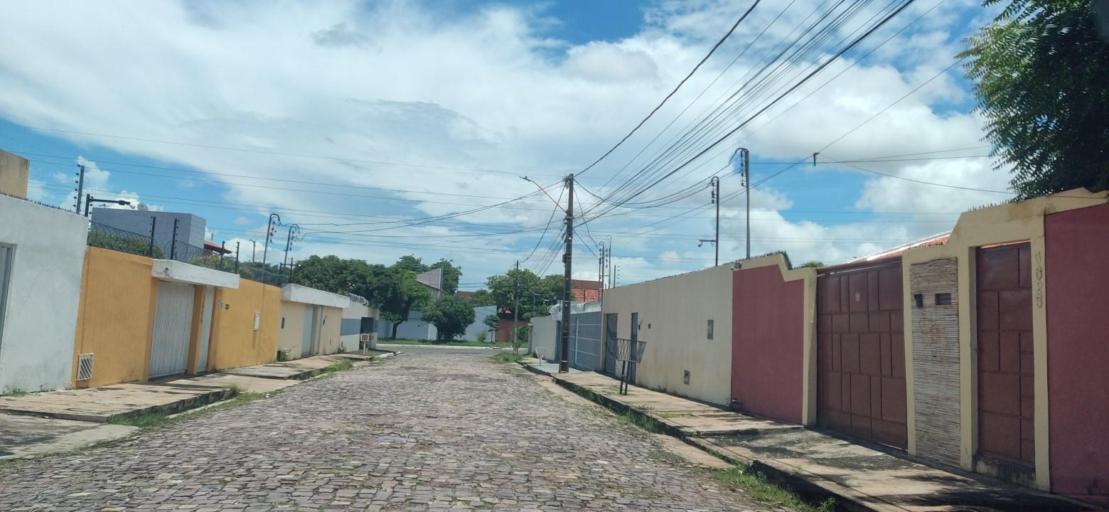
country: BR
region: Piaui
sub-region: Teresina
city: Teresina
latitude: -5.0711
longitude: -42.7508
